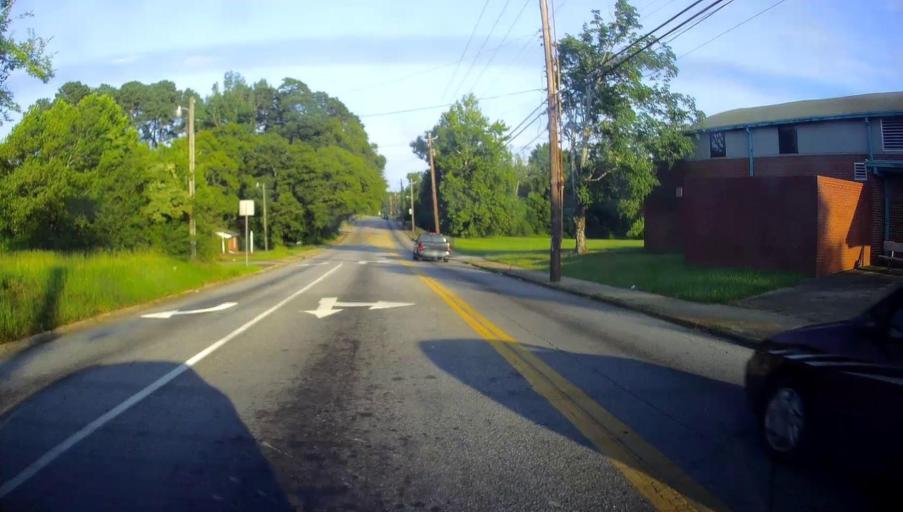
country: US
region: Georgia
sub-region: Bibb County
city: Macon
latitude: 32.8588
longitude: -83.6918
